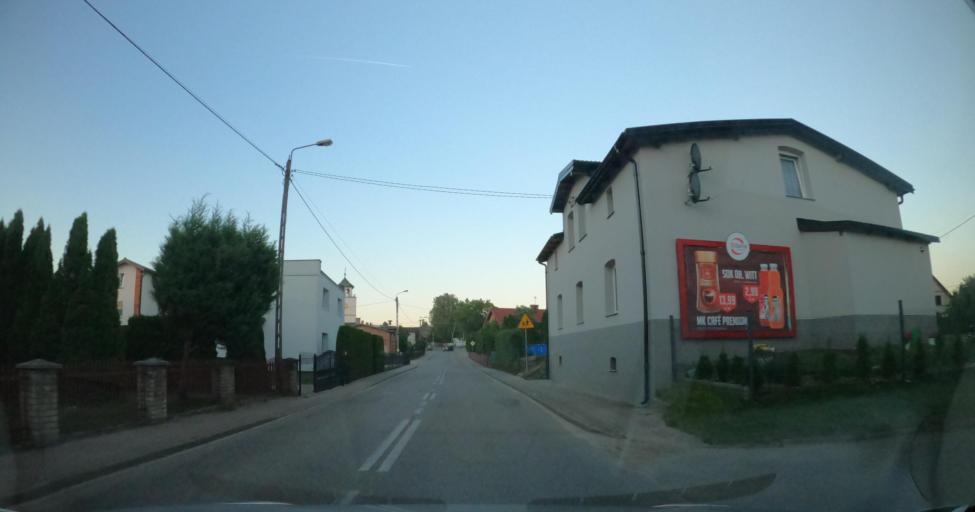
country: PL
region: Pomeranian Voivodeship
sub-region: Powiat wejherowski
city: Linia
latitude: 54.4513
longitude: 17.9326
